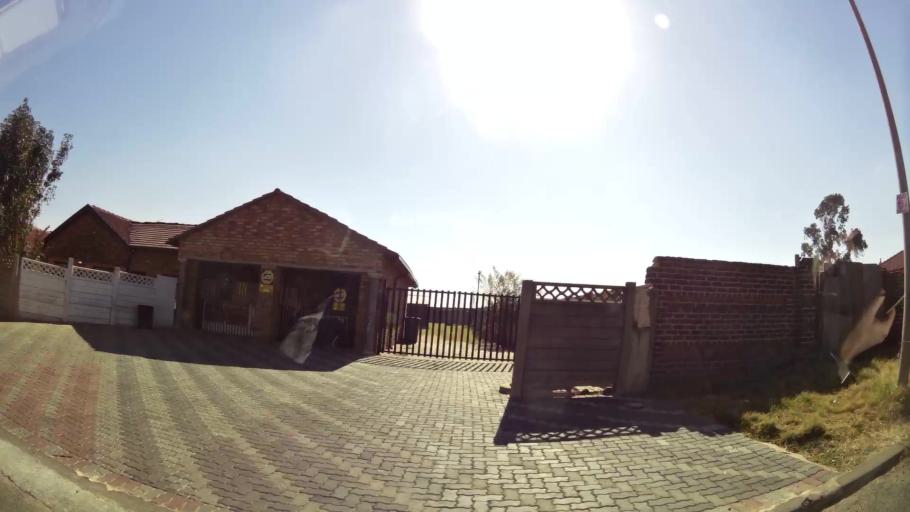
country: ZA
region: Gauteng
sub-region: Ekurhuleni Metropolitan Municipality
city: Tembisa
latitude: -26.0356
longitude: 28.2249
